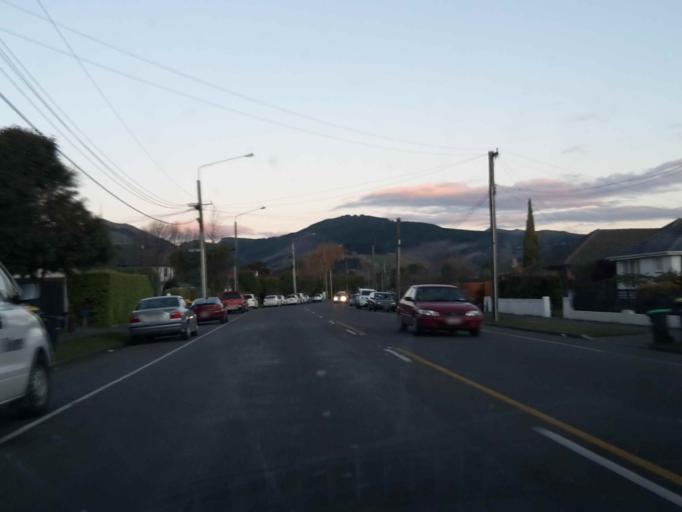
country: NZ
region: Canterbury
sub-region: Christchurch City
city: Christchurch
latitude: -43.5652
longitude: 172.6095
